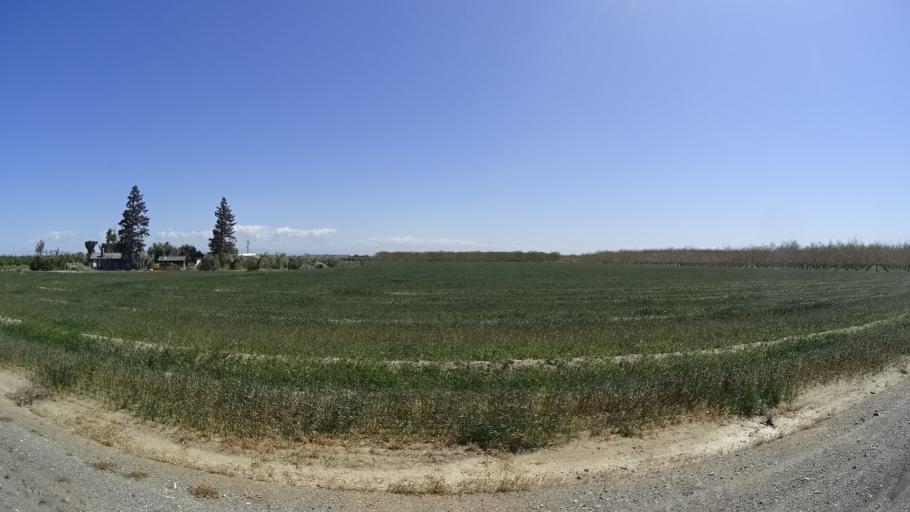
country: US
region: California
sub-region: Glenn County
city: Orland
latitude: 39.7044
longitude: -122.1547
